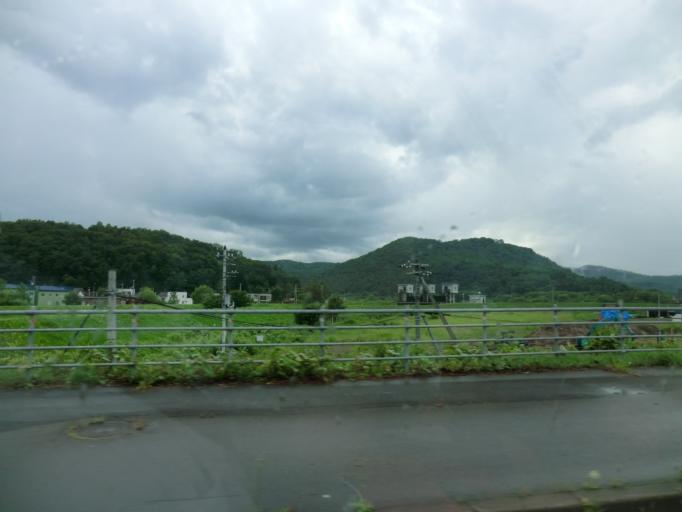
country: JP
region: Hokkaido
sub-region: Asahikawa-shi
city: Asahikawa
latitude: 43.7838
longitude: 142.3122
